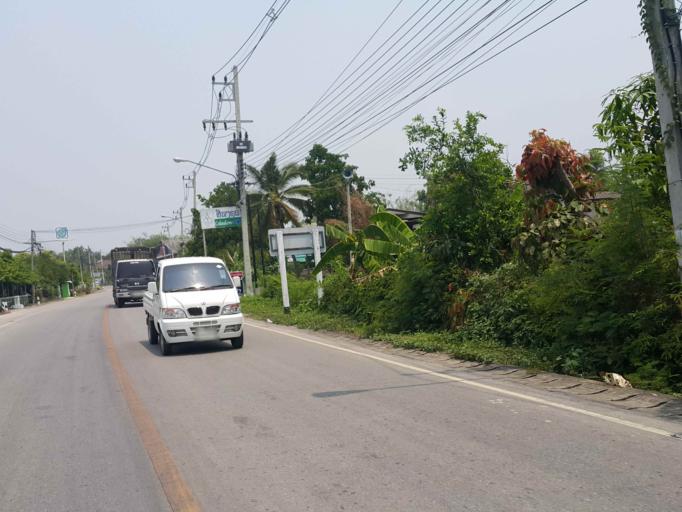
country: TH
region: Chiang Mai
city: San Sai
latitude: 18.8464
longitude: 99.1316
